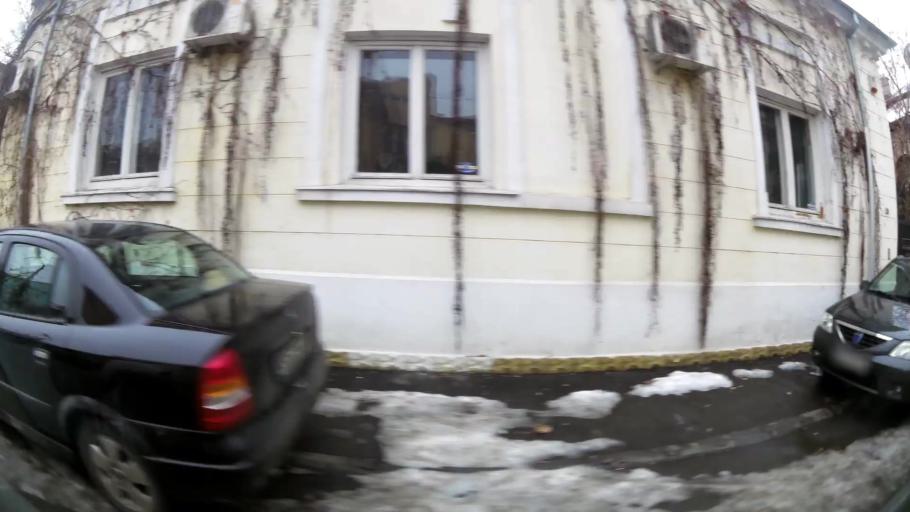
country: RO
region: Bucuresti
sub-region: Municipiul Bucuresti
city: Bucharest
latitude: 44.4408
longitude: 26.1107
